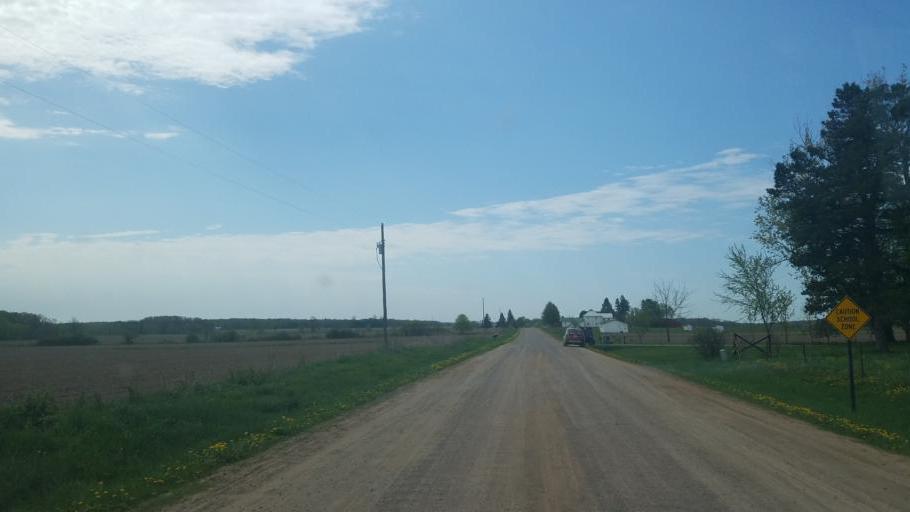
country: US
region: Wisconsin
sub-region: Marathon County
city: Spencer
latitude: 44.6395
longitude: -90.3772
